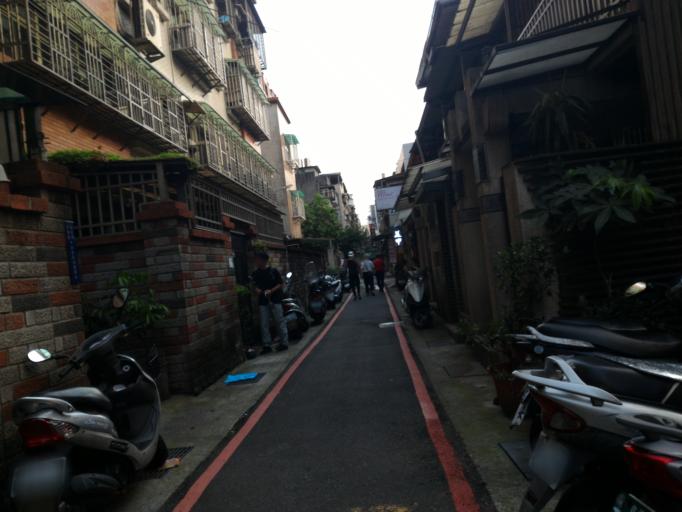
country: TW
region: Taipei
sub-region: Taipei
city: Banqiao
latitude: 25.0029
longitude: 121.5123
